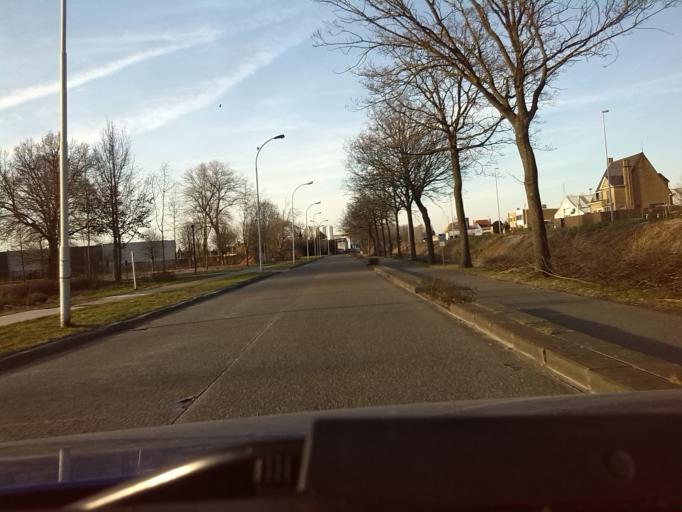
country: BE
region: Flanders
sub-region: Provincie West-Vlaanderen
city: Brugge
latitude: 51.2276
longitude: 3.2139
